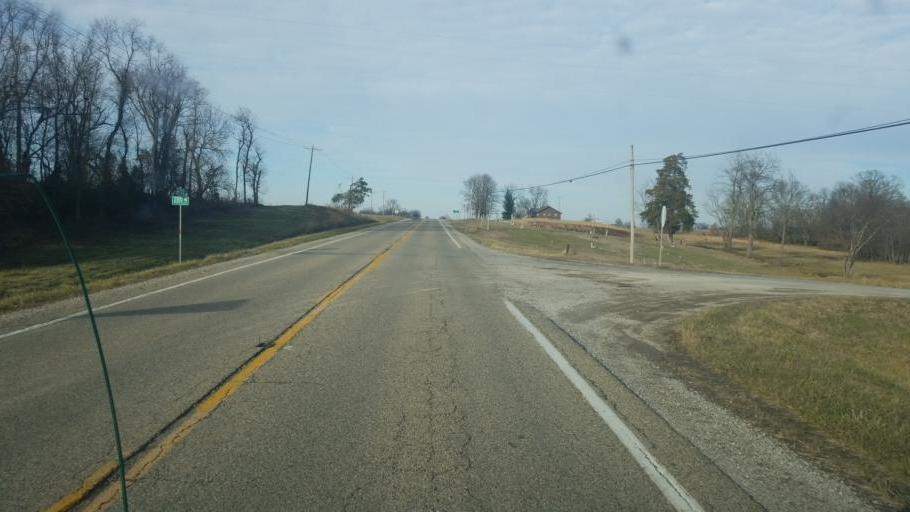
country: US
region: Illinois
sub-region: Lawrence County
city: Bridgeport
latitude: 38.6093
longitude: -87.6943
